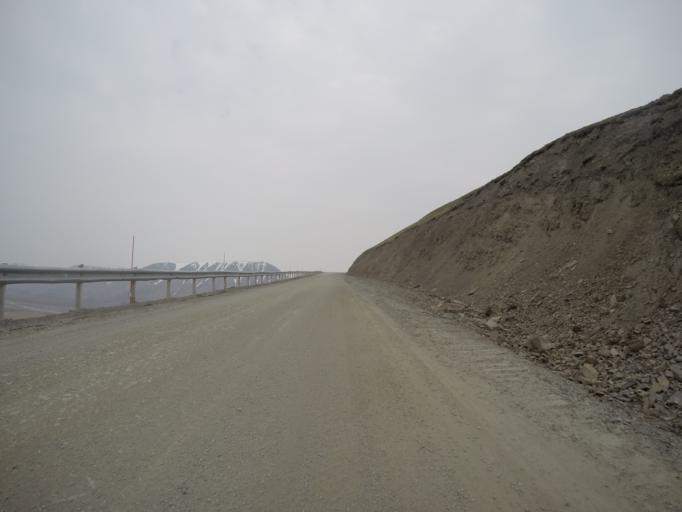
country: SJ
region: Svalbard
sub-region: Spitsbergen
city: Longyearbyen
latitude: 78.1603
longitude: 16.0037
